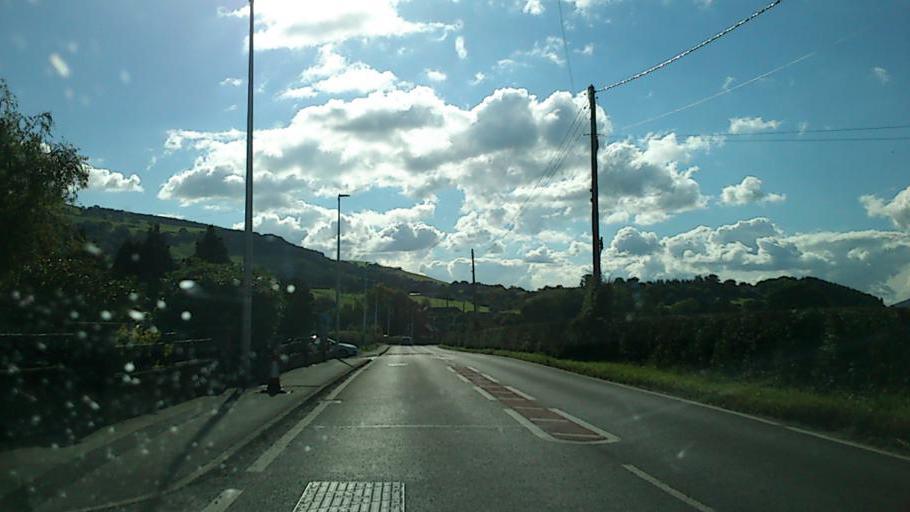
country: GB
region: Wales
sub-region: Sir Powys
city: Welshpool
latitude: 52.6917
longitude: -3.0724
